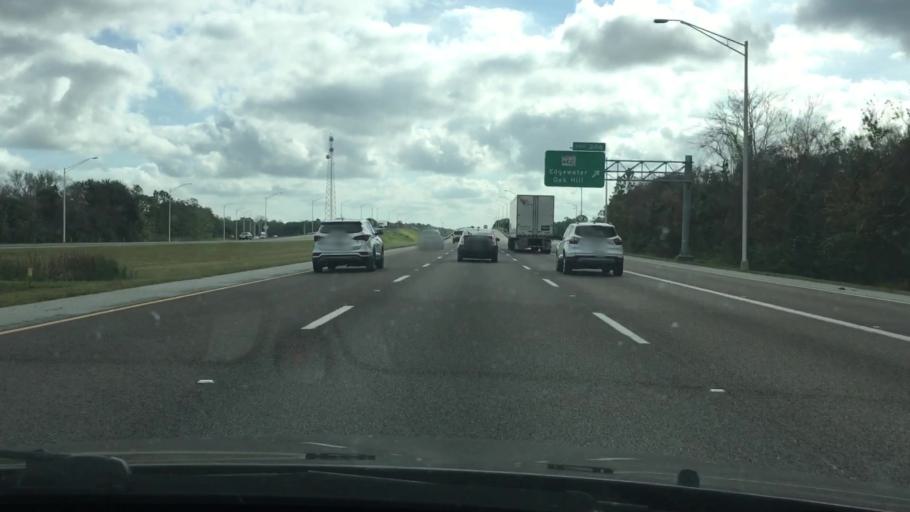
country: US
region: Florida
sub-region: Volusia County
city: Edgewater
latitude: 28.9553
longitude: -80.9530
